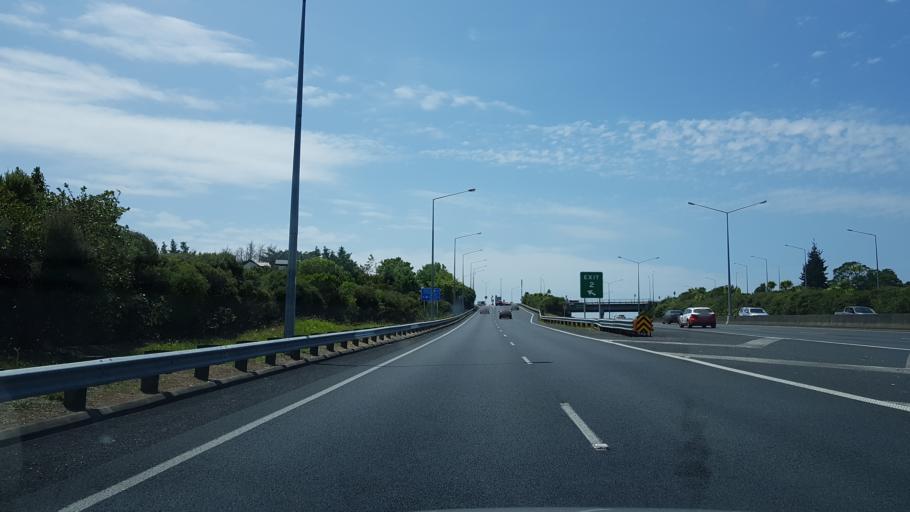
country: NZ
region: Auckland
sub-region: Auckland
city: Rothesay Bay
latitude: -36.7599
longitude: 174.7013
